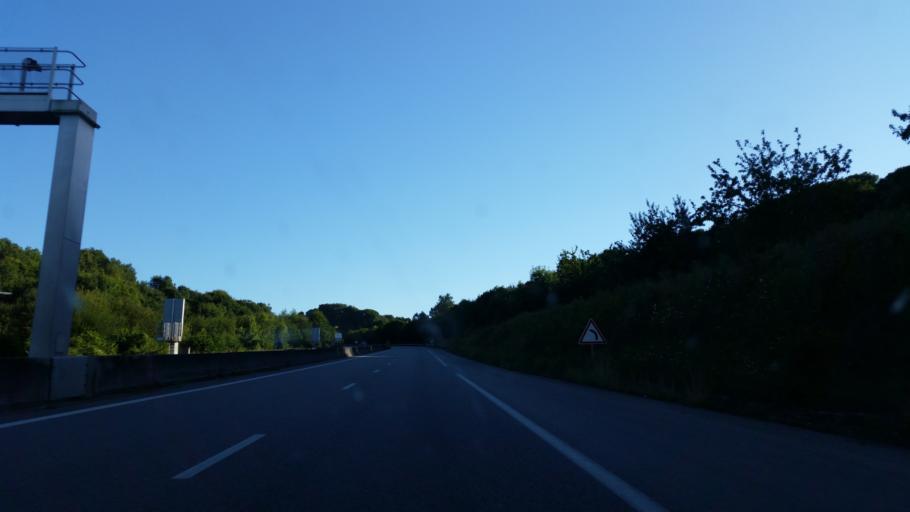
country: FR
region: Lower Normandy
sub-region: Departement du Calvados
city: La Riviere-Saint-Sauveur
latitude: 49.4044
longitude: 0.2637
